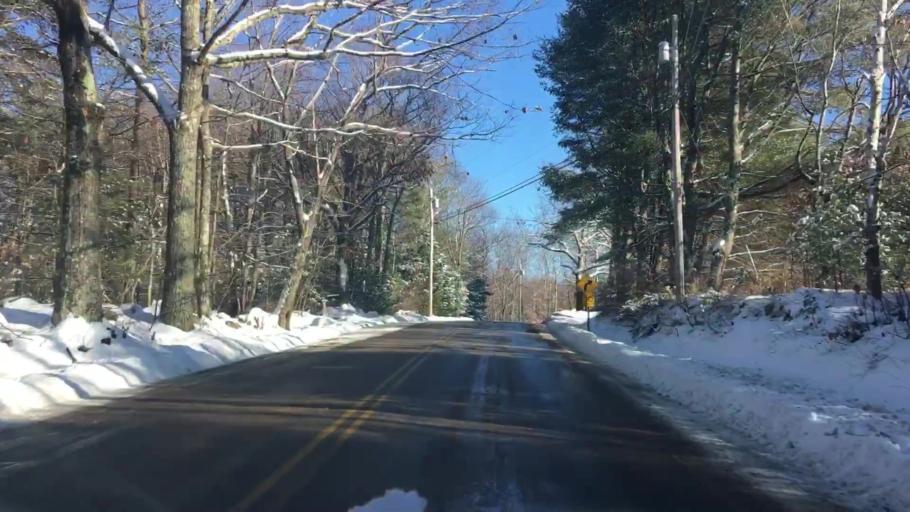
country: US
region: Maine
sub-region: Cumberland County
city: New Gloucester
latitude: 43.9574
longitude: -70.3216
